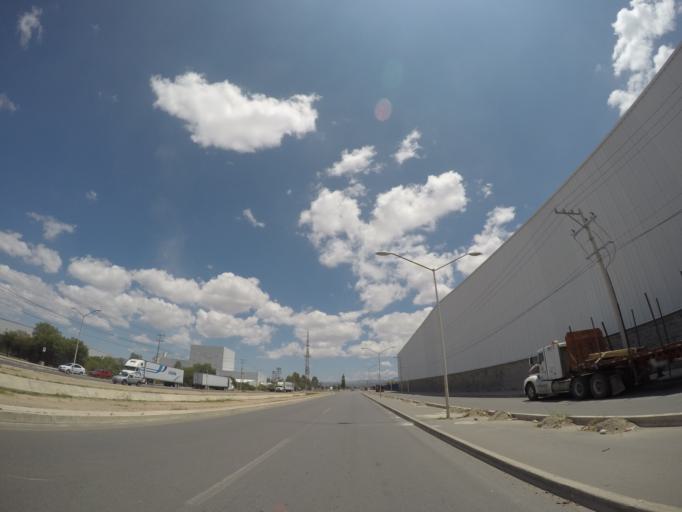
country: MX
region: San Luis Potosi
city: La Pila
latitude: 22.0500
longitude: -100.8674
